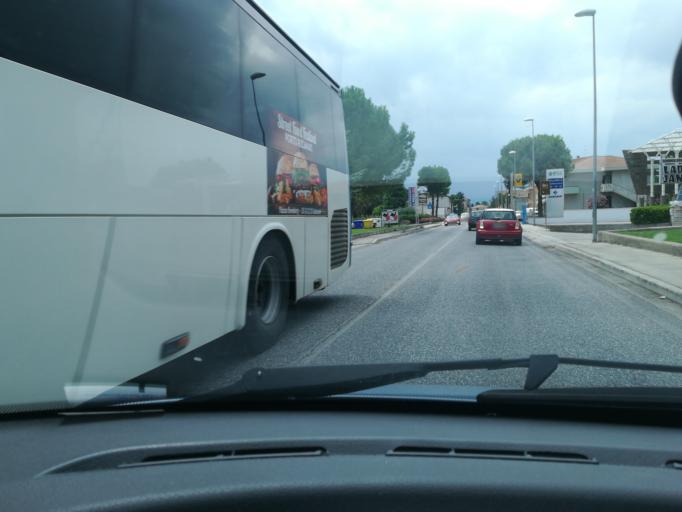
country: IT
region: The Marches
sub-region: Provincia di Macerata
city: Montecassiano
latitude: 43.3566
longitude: 13.4839
